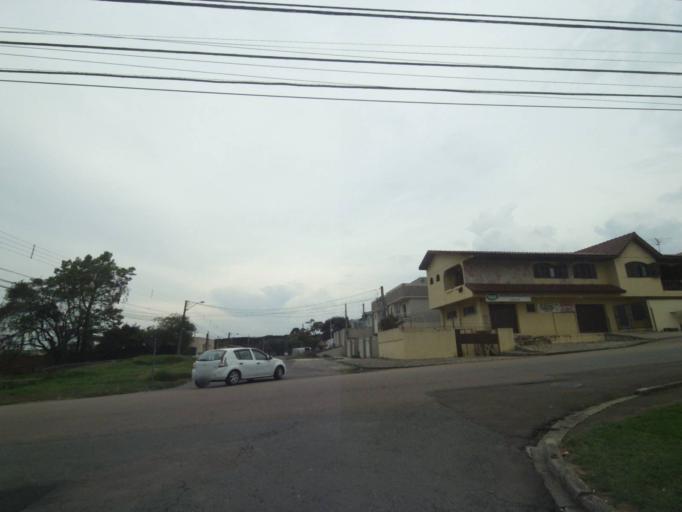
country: BR
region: Parana
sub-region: Pinhais
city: Pinhais
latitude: -25.3982
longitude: -49.2015
